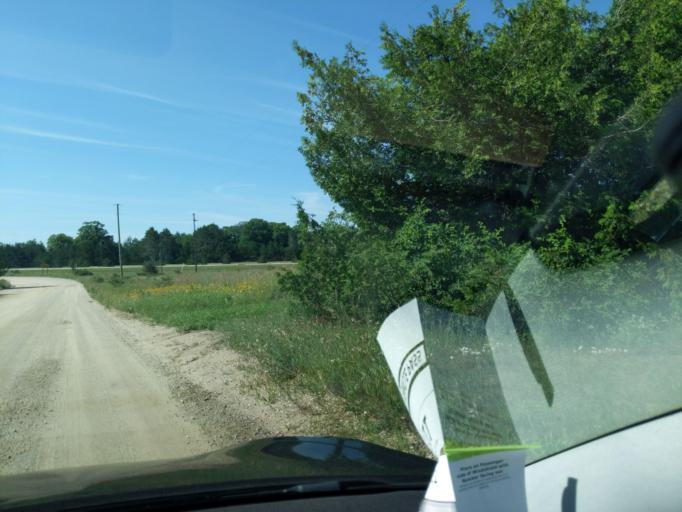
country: US
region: Michigan
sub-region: Cheboygan County
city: Cheboygan
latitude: 45.6683
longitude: -84.6510
